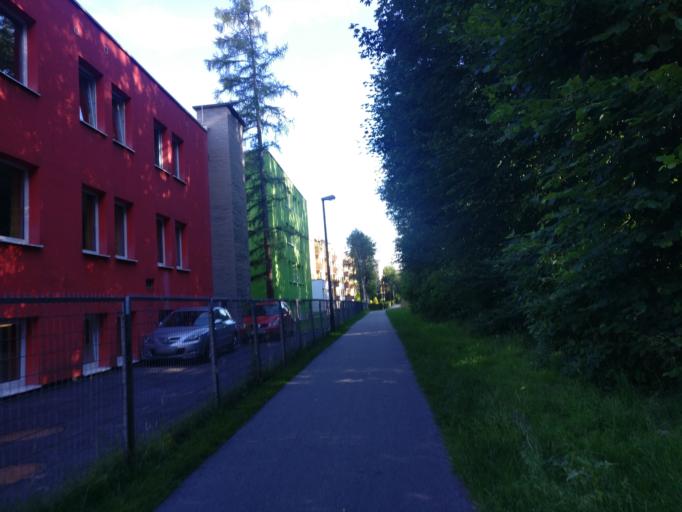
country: AT
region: Salzburg
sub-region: Politischer Bezirk Salzburg-Umgebung
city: Anif
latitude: 47.7789
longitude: 13.0724
